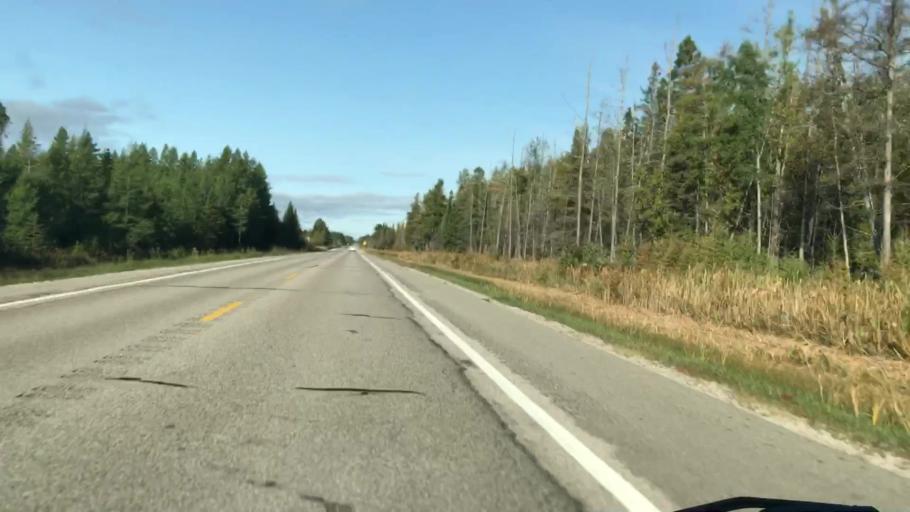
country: US
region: Michigan
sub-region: Luce County
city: Newberry
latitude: 46.3036
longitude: -85.3143
